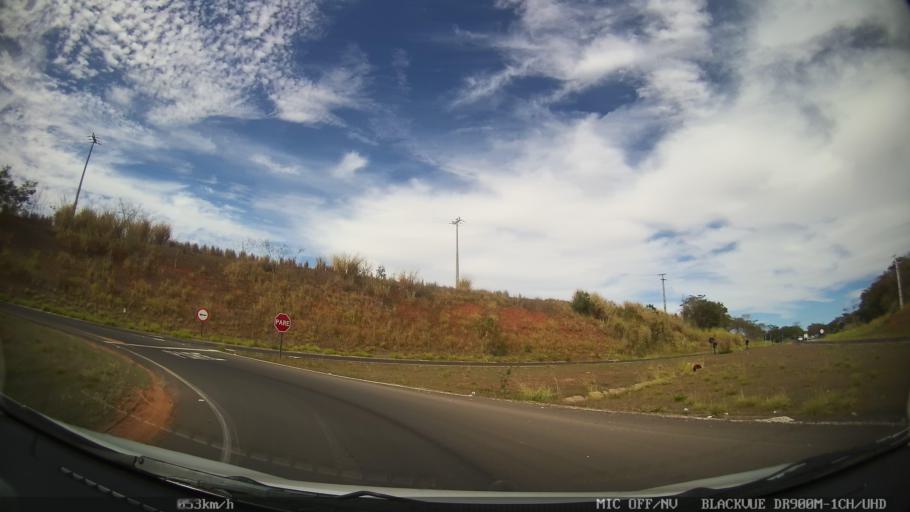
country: BR
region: Sao Paulo
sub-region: Catanduva
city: Catanduva
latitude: -21.1656
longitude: -48.9884
